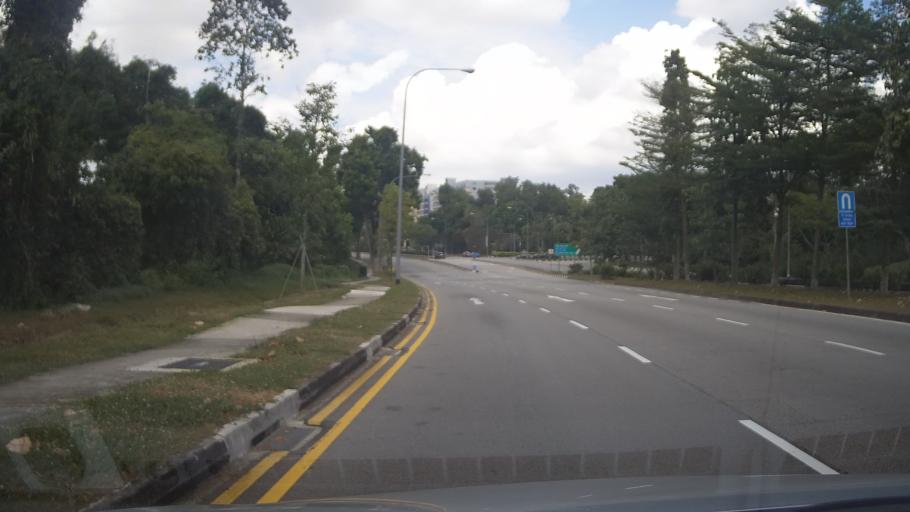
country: SG
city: Singapore
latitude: 1.3247
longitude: 103.7583
